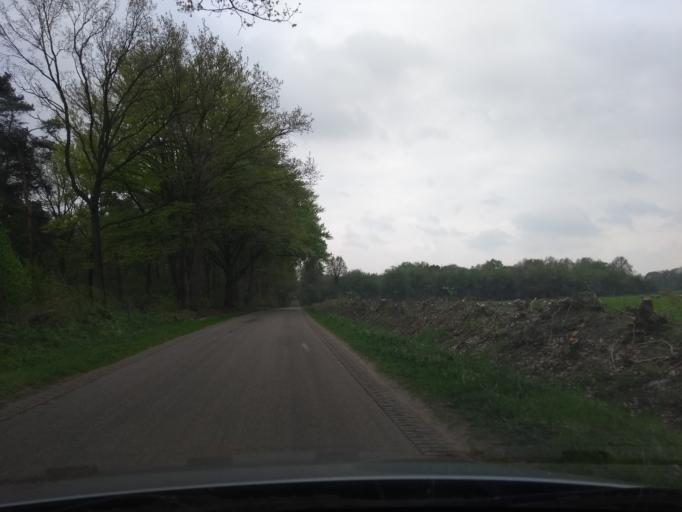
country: DE
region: Lower Saxony
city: Getelo
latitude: 52.4271
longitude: 6.9070
